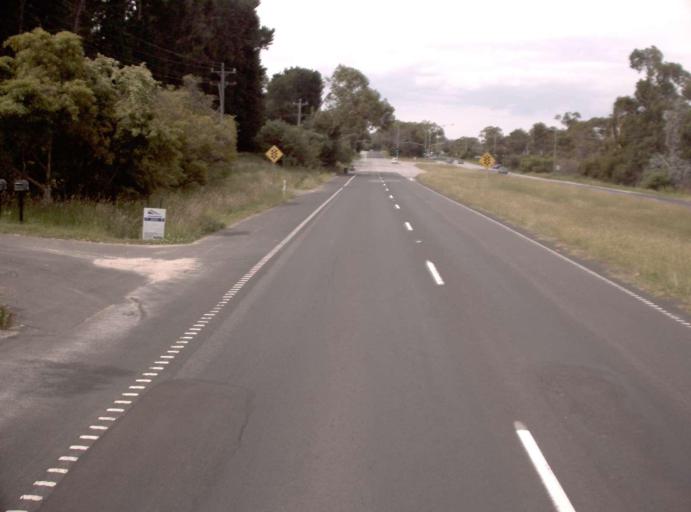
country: AU
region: Victoria
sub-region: Mornington Peninsula
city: Baxter
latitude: -38.1974
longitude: 145.1317
